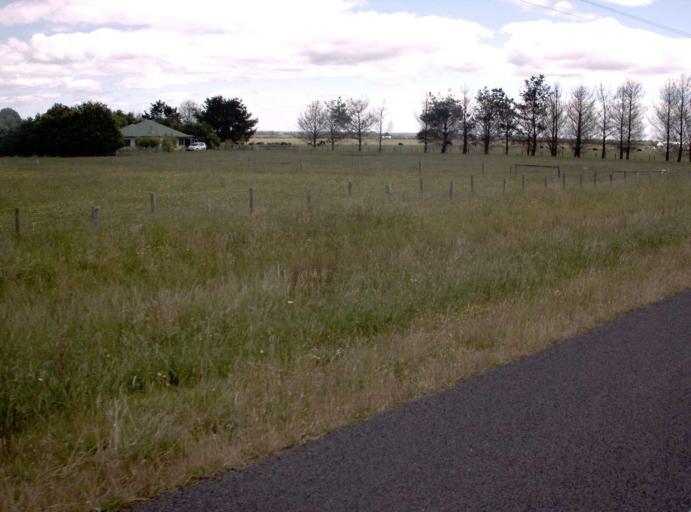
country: AU
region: Victoria
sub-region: Bass Coast
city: North Wonthaggi
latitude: -38.4680
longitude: 145.4771
